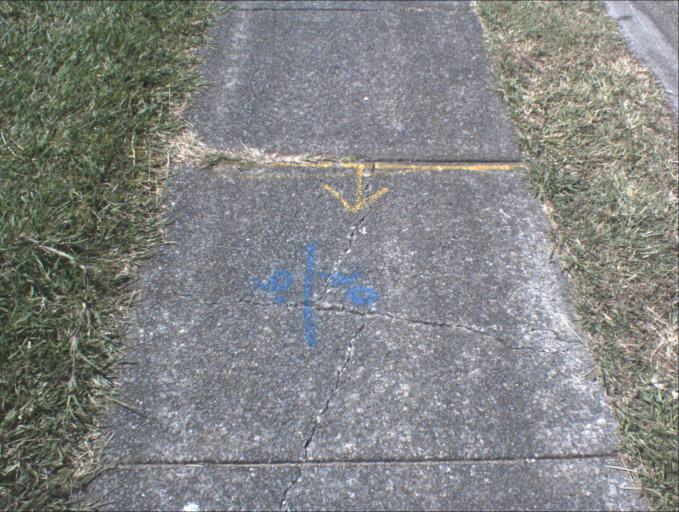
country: AU
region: Queensland
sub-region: Logan
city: Springwood
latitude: -27.6102
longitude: 153.1153
